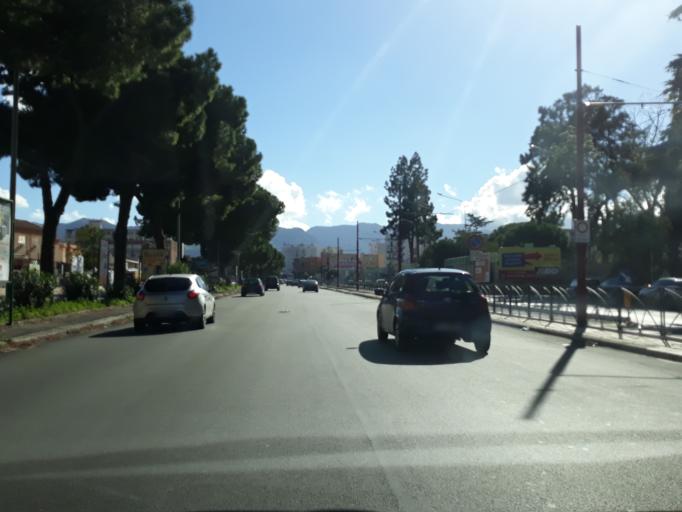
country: IT
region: Sicily
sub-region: Palermo
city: Palermo
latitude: 38.1231
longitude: 13.3290
